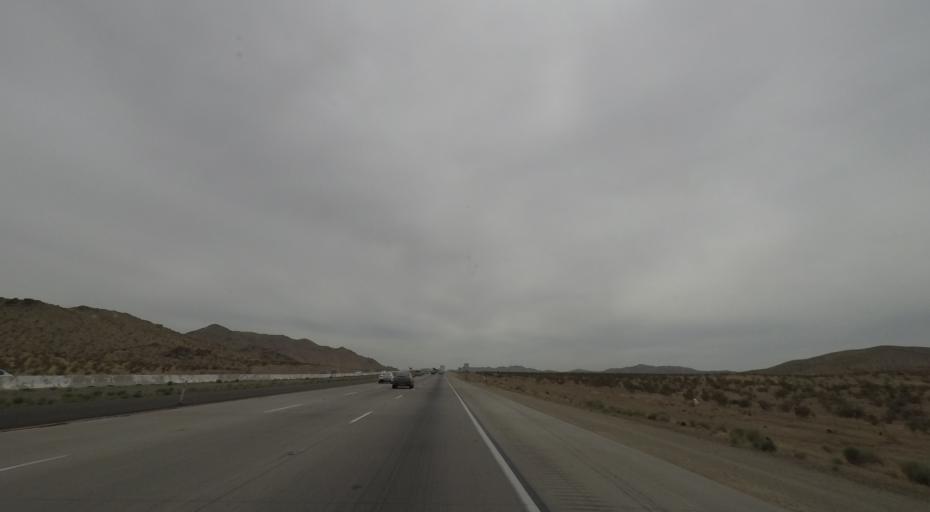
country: US
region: California
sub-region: San Bernardino County
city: Lenwood
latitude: 34.7465
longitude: -117.1728
